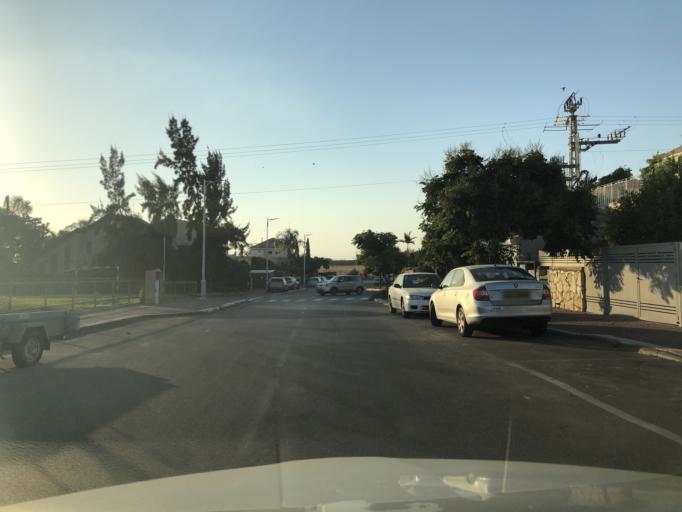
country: PS
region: West Bank
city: Hablah
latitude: 32.1601
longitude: 34.9691
